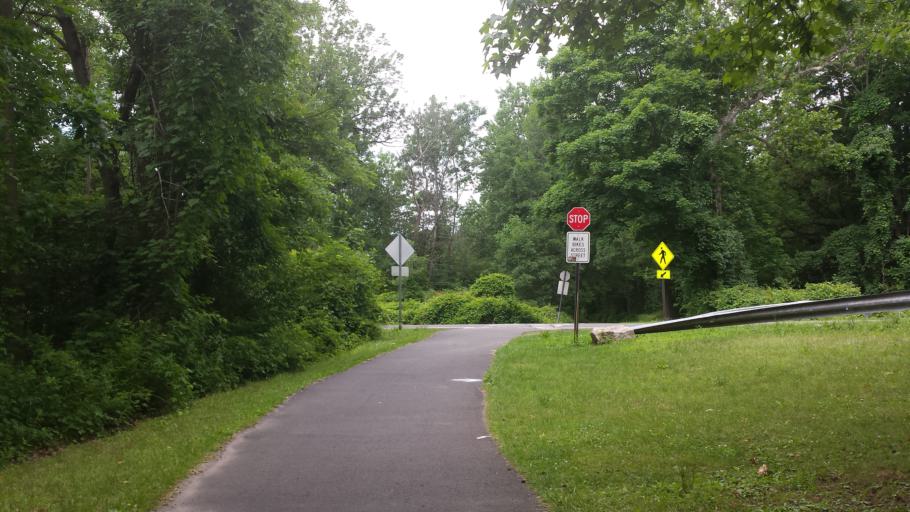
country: US
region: New York
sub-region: Westchester County
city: Valhalla
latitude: 41.0616
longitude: -73.7736
